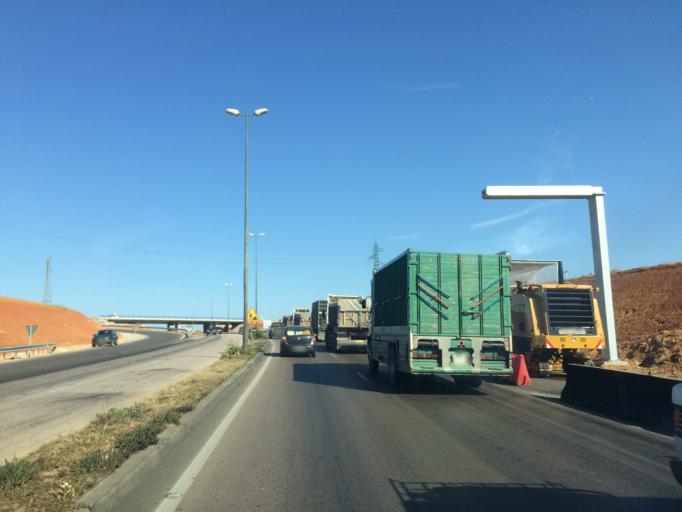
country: MA
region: Rabat-Sale-Zemmour-Zaer
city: Sale
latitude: 33.9826
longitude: -6.7431
